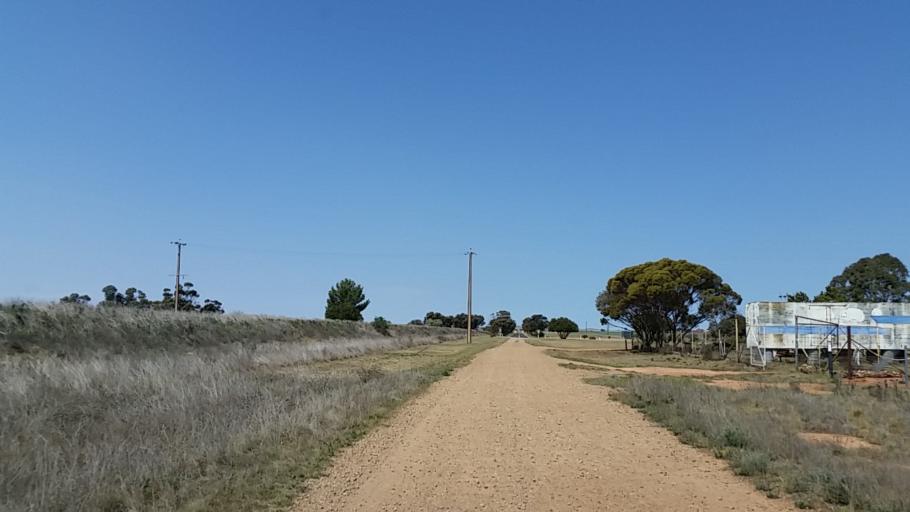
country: AU
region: South Australia
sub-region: Peterborough
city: Peterborough
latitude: -32.9764
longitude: 138.8451
